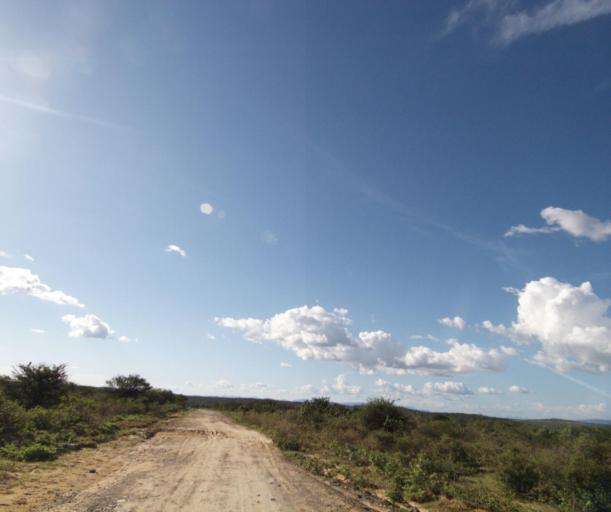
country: BR
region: Bahia
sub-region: Tanhacu
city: Tanhacu
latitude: -14.1841
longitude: -40.9982
